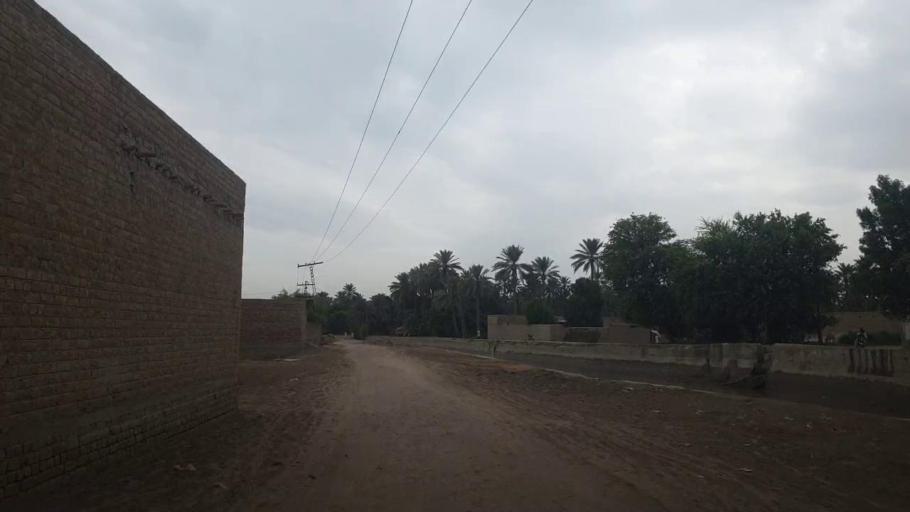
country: PK
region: Sindh
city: Khairpur
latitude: 27.5709
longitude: 68.7467
